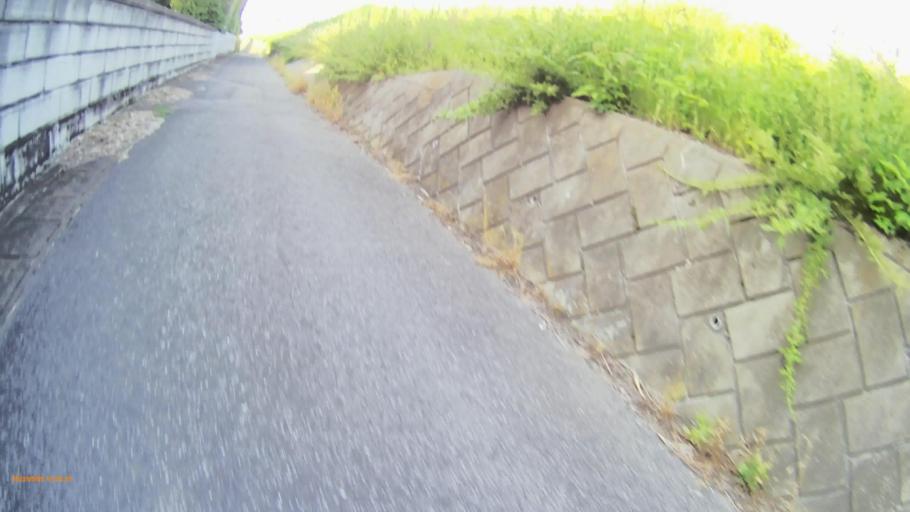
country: JP
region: Saitama
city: Kurihashi
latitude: 36.1189
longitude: 139.7189
